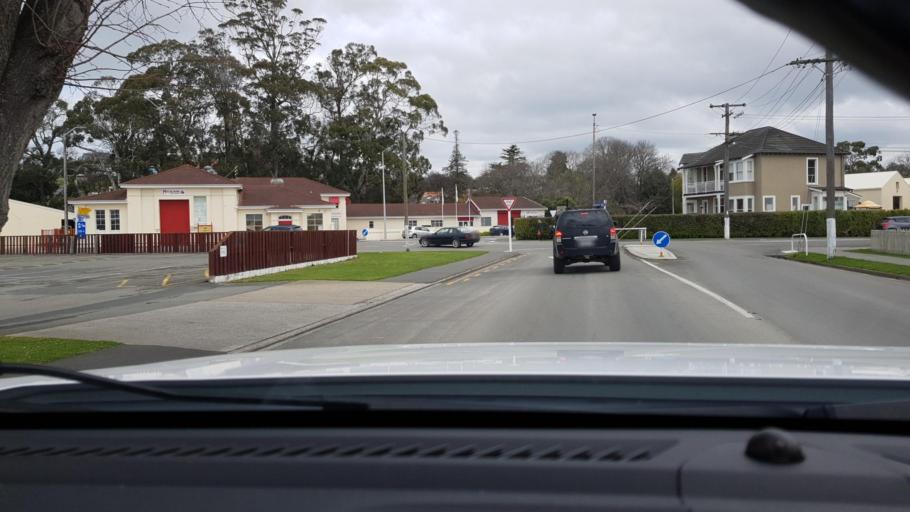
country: NZ
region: Otago
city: Oamaru
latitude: -45.0979
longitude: 170.9662
